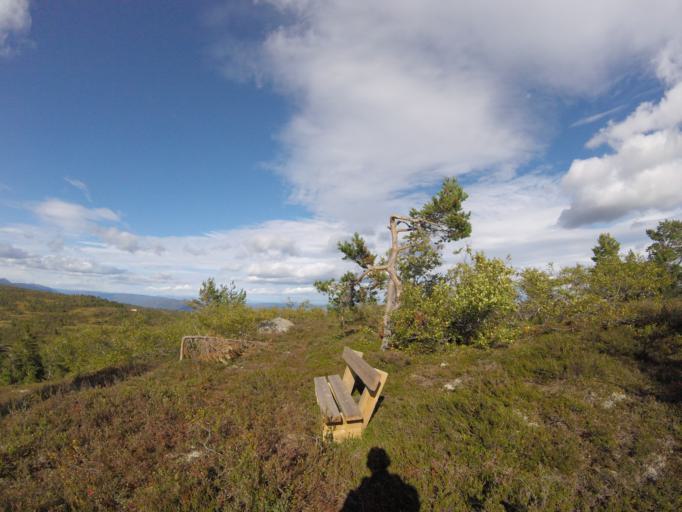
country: NO
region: Buskerud
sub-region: Flesberg
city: Lampeland
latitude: 59.7617
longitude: 9.4258
